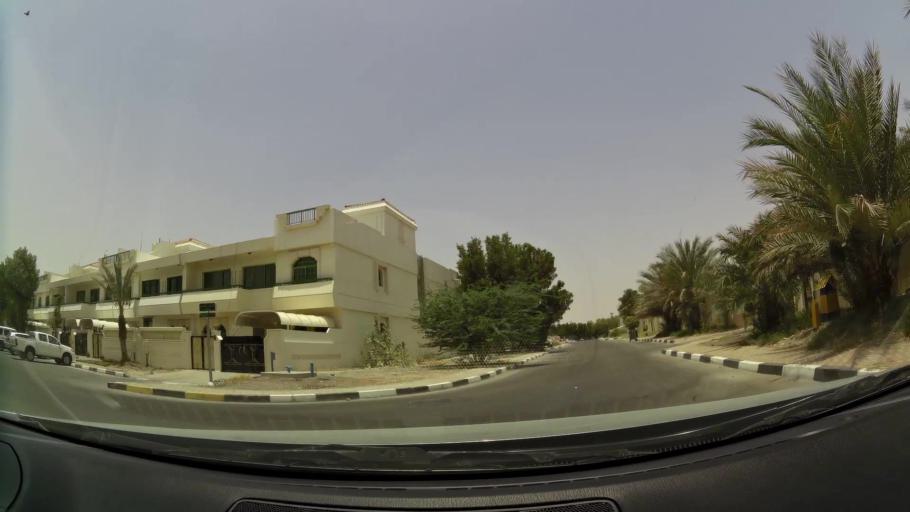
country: AE
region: Abu Dhabi
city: Al Ain
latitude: 24.2068
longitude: 55.7493
